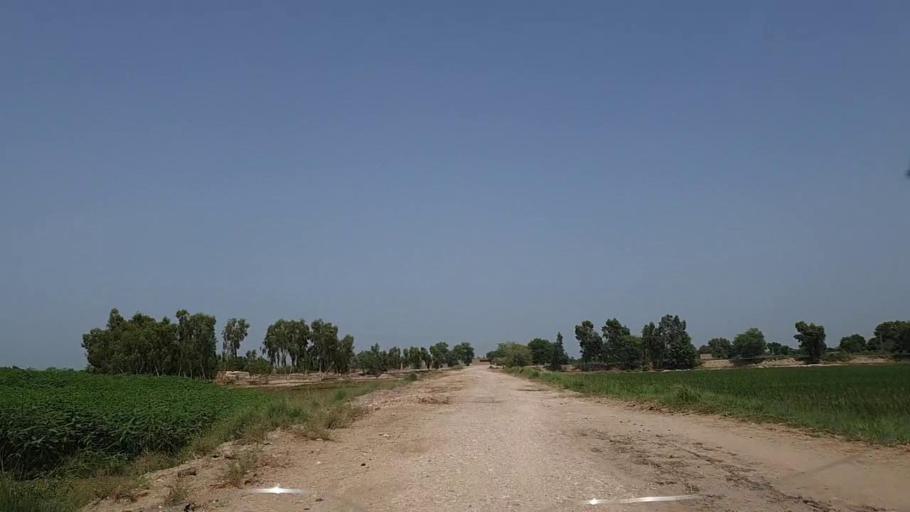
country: PK
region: Sindh
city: Tharu Shah
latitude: 27.0143
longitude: 68.1430
